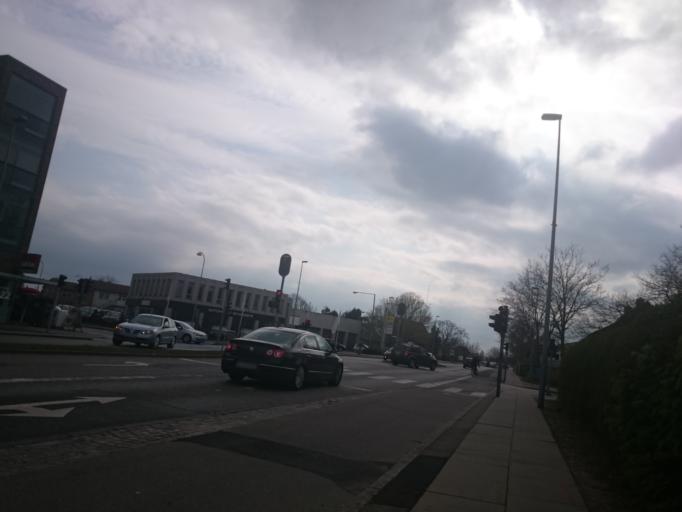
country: DK
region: Capital Region
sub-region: Gladsaxe Municipality
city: Buddinge
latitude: 55.7603
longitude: 12.4521
